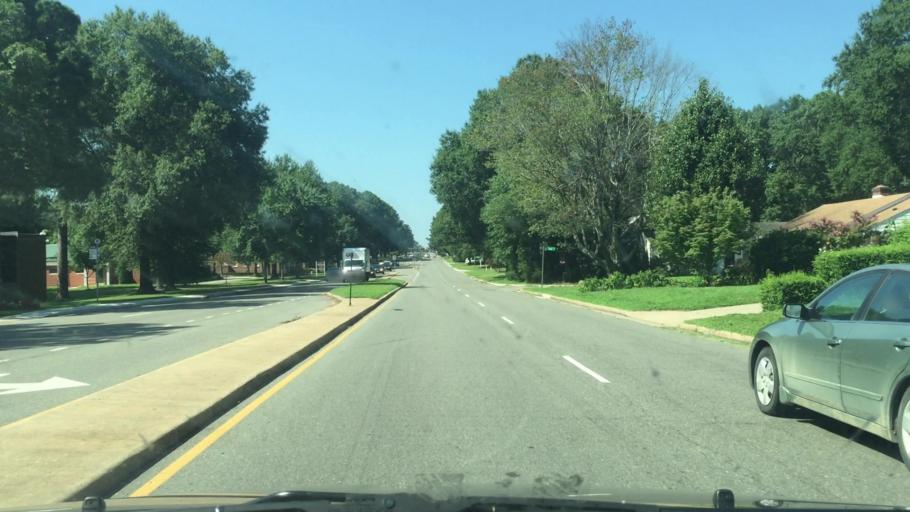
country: US
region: Virginia
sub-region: Henrico County
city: Dumbarton
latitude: 37.5891
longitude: -77.5049
